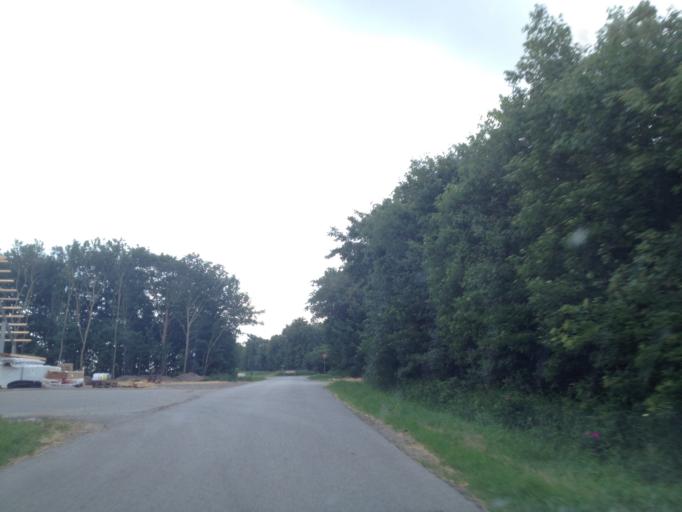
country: DK
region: South Denmark
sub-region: Tonder Kommune
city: Sherrebek
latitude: 55.1745
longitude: 8.7214
